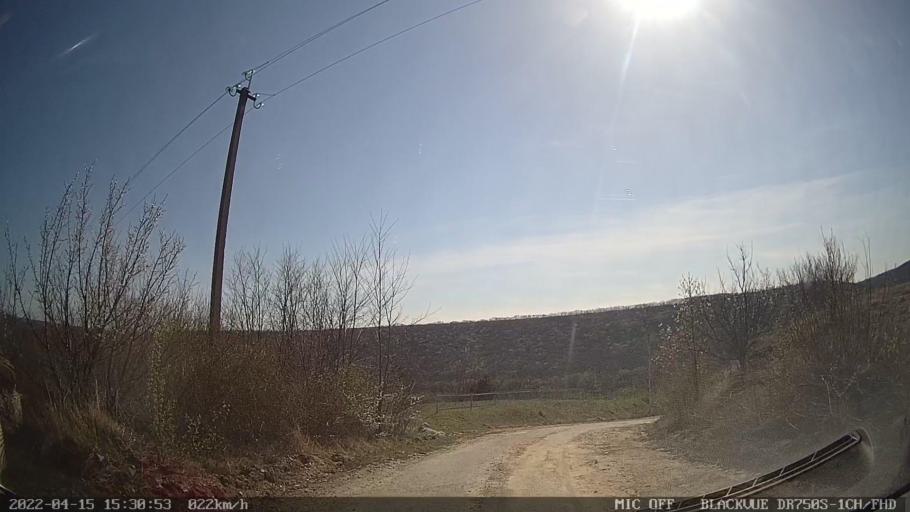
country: MD
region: Raionul Ocnita
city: Otaci
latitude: 48.3537
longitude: 27.9229
